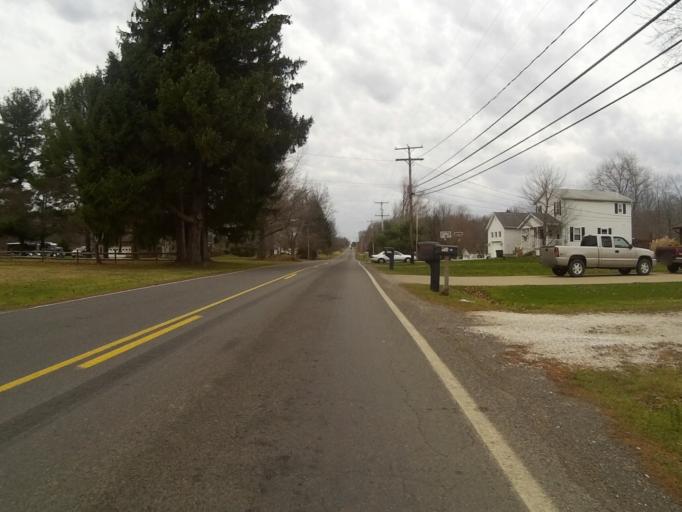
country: US
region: Ohio
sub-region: Portage County
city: Brimfield
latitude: 41.0827
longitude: -81.3293
